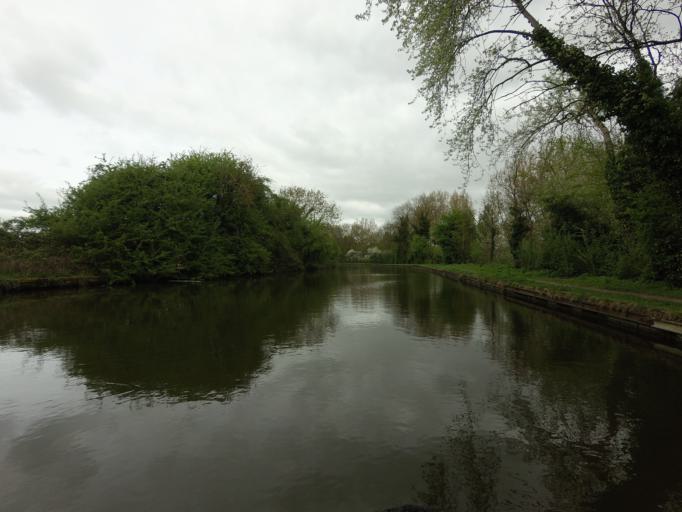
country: GB
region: England
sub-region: Milton Keynes
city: Simpson
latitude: 52.0074
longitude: -0.7169
